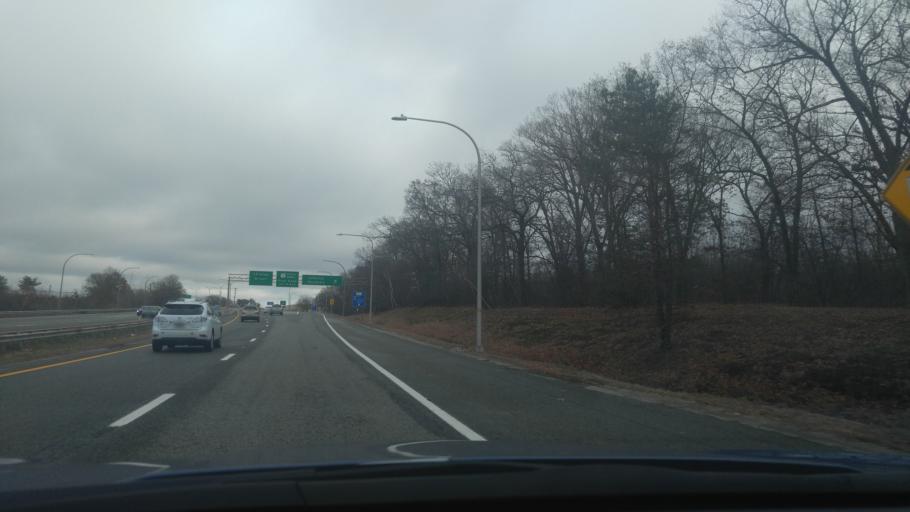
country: US
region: Rhode Island
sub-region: Kent County
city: Warwick
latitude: 41.7249
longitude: -71.4501
